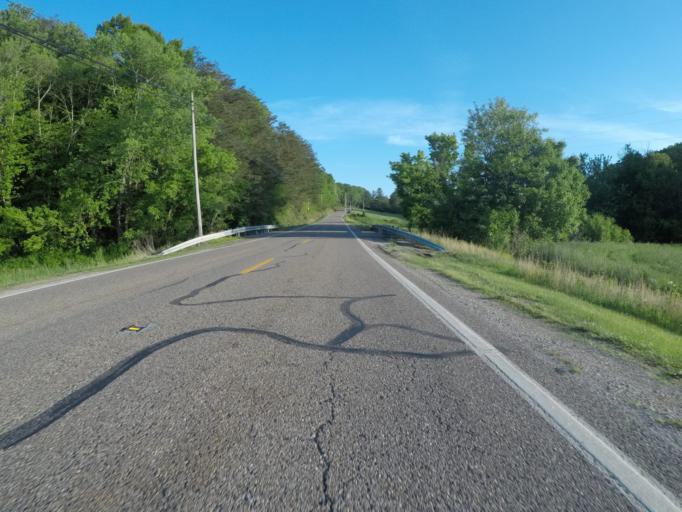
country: US
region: West Virginia
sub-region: Cabell County
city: Huntington
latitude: 38.5528
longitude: -82.4629
